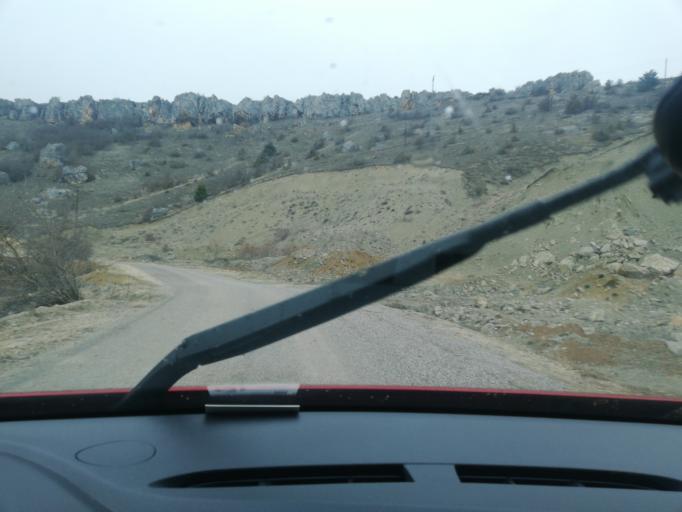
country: TR
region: Kastamonu
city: Seydiler
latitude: 41.6244
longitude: 33.7244
